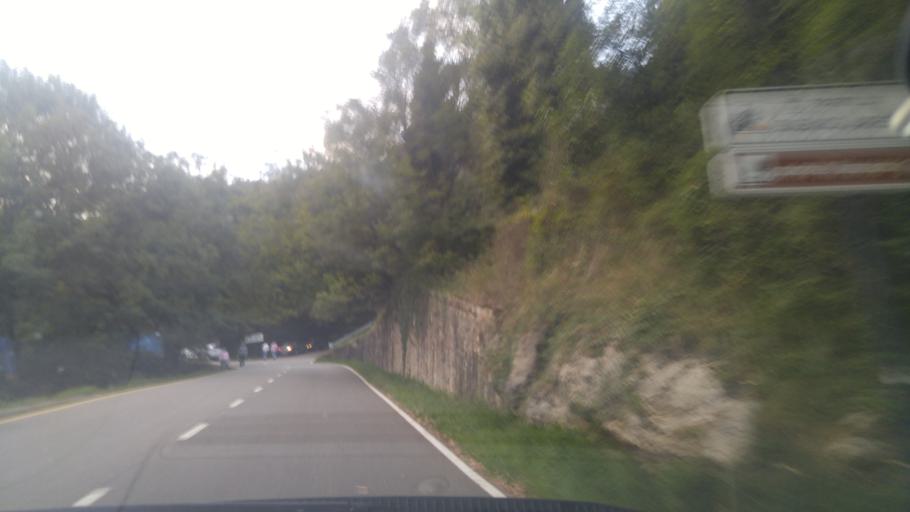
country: ES
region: Asturias
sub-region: Province of Asturias
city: Oviedo
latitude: 43.3800
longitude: -5.8673
